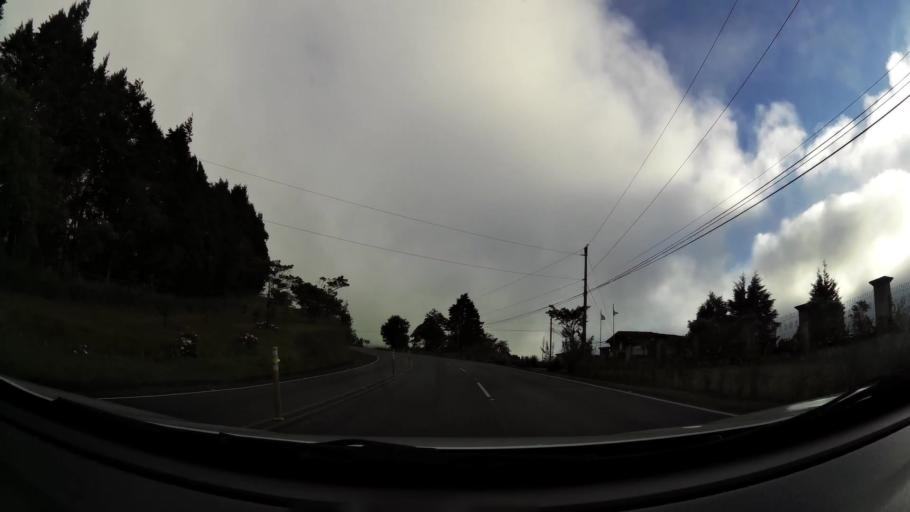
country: CR
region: Heredia
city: Angeles
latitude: 10.0314
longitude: -84.0032
